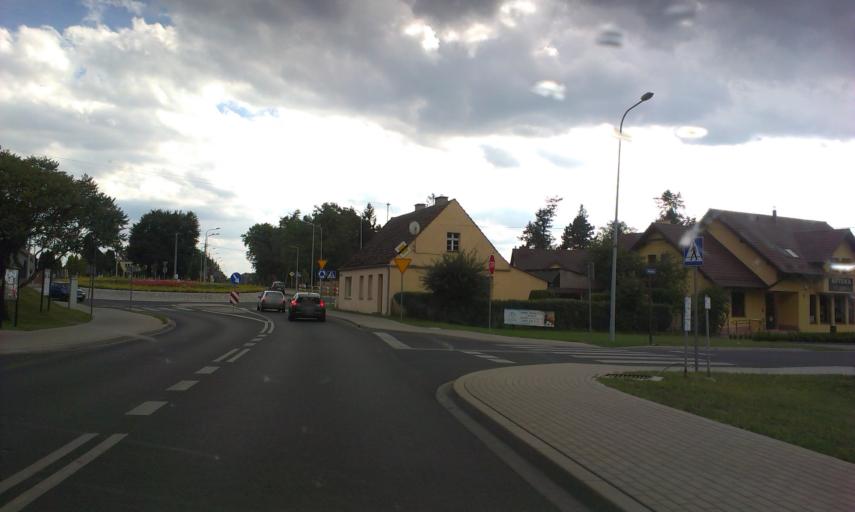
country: PL
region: Greater Poland Voivodeship
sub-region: Powiat zlotowski
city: Krajenka
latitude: 53.2952
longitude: 16.9894
